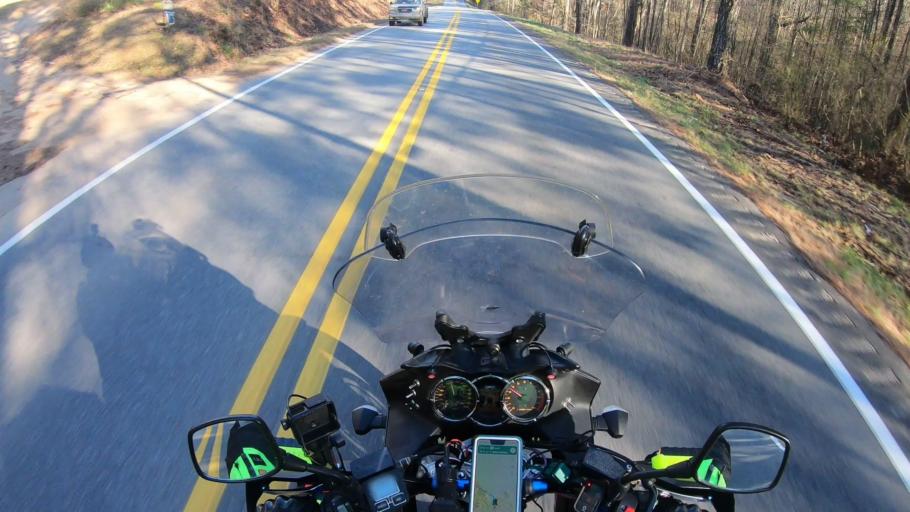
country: US
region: Alabama
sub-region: Cleburne County
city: Heflin
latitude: 33.6690
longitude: -85.5643
